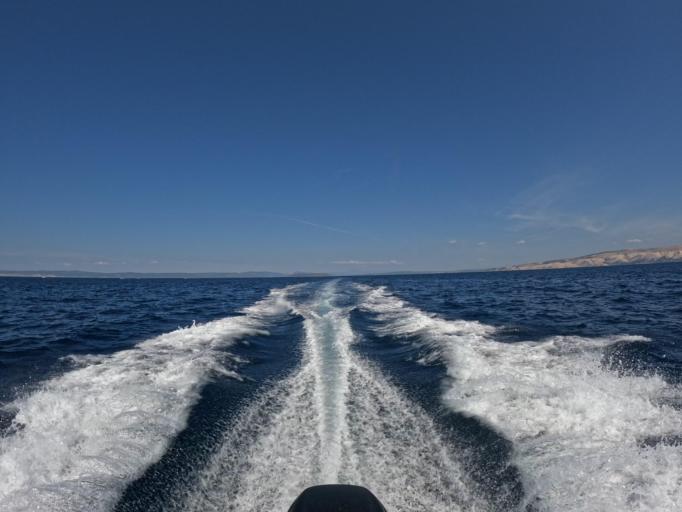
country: HR
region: Primorsko-Goranska
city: Lopar
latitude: 44.8830
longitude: 14.6545
